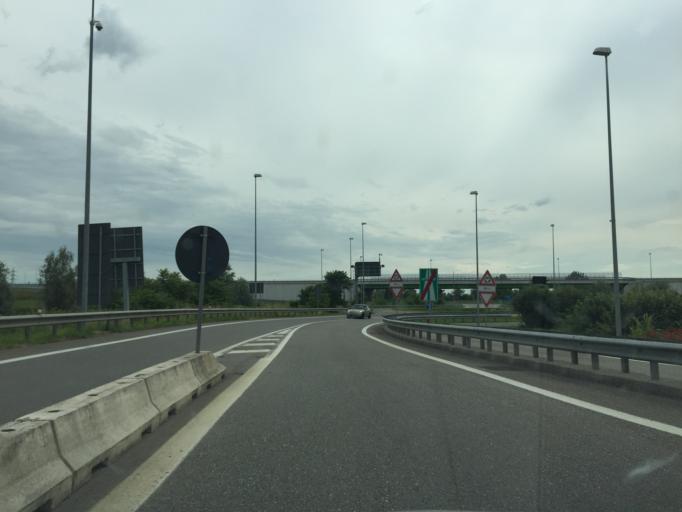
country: IT
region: Lombardy
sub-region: Provincia di Brescia
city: Montirone
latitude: 45.4673
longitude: 10.2157
